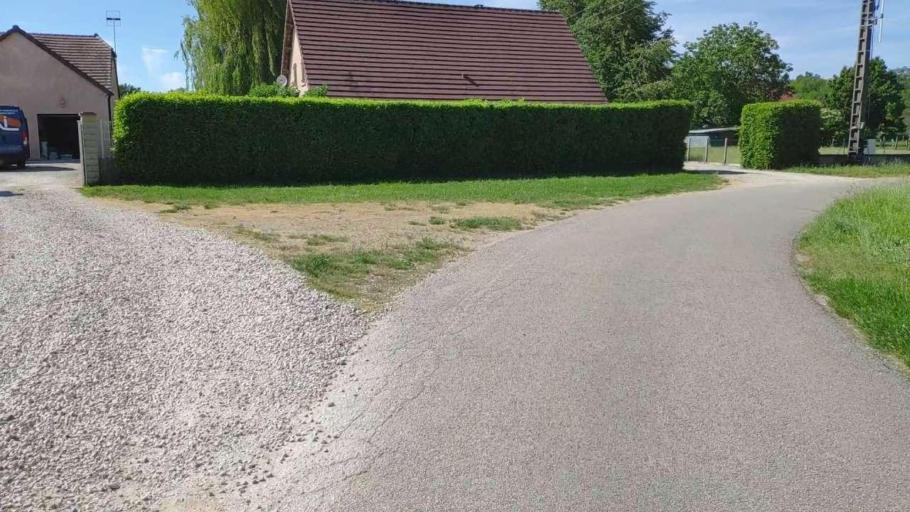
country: FR
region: Franche-Comte
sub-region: Departement du Jura
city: Bletterans
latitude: 46.7638
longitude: 5.4713
